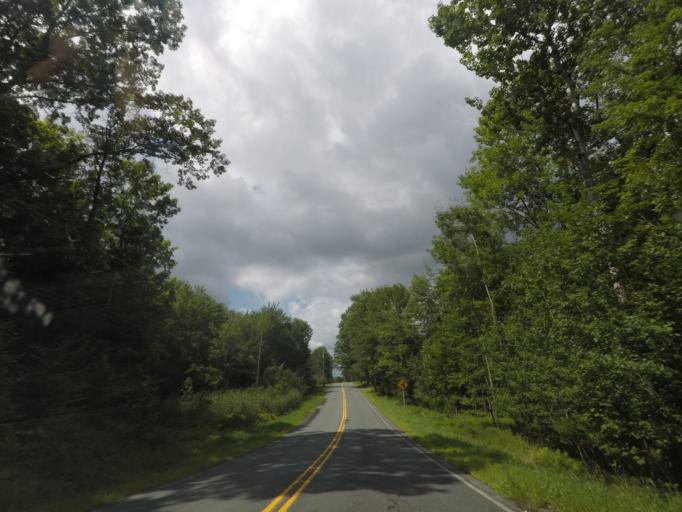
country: US
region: New York
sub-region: Rensselaer County
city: Averill Park
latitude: 42.6513
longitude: -73.5017
